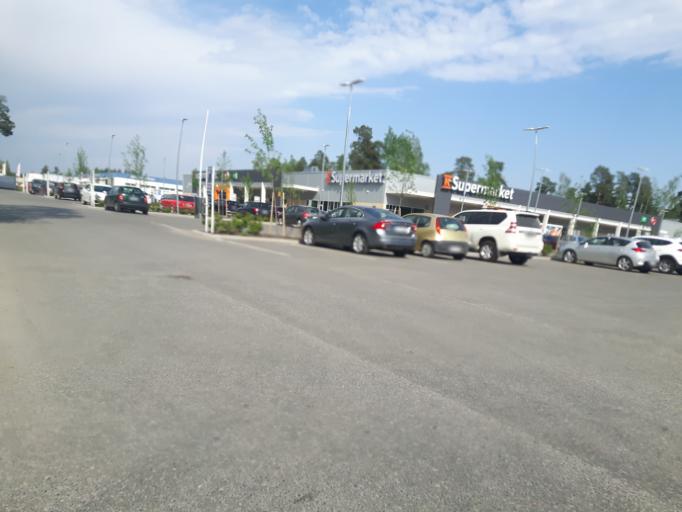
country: FI
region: Uusimaa
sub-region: Porvoo
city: Porvoo
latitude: 60.3993
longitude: 25.6845
